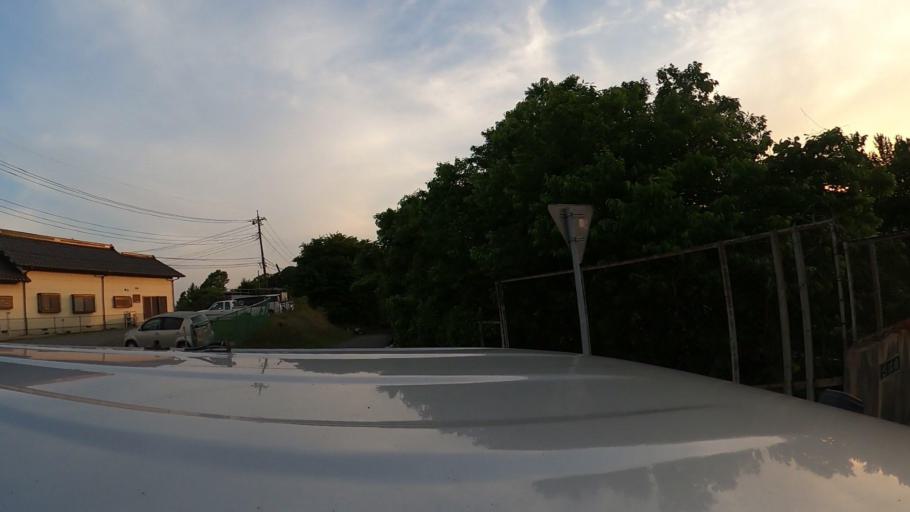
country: JP
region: Ibaraki
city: Ushiku
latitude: 36.0303
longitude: 140.0877
